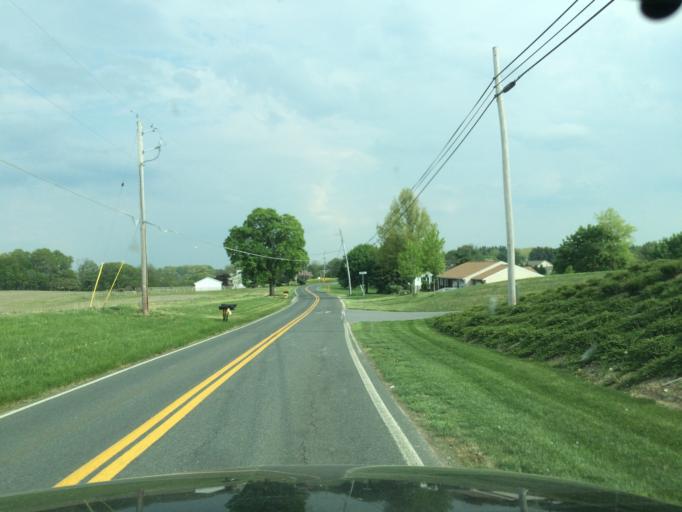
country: US
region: Maryland
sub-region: Carroll County
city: Eldersburg
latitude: 39.4375
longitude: -77.0182
